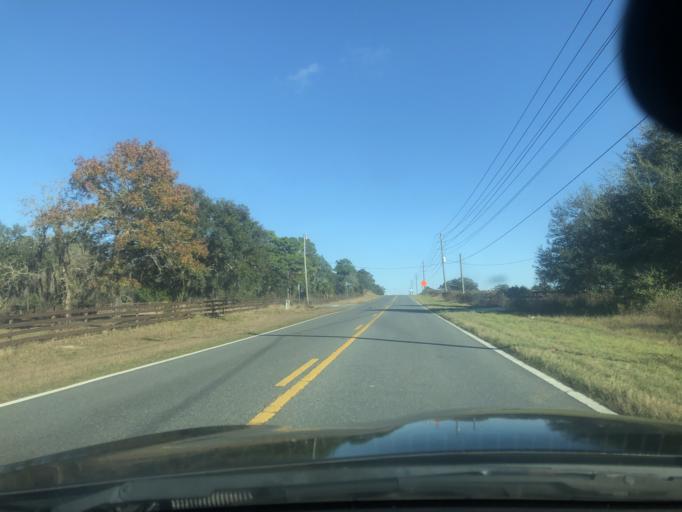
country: US
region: Florida
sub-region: Citrus County
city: Sugarmill Woods
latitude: 28.7640
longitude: -82.5251
